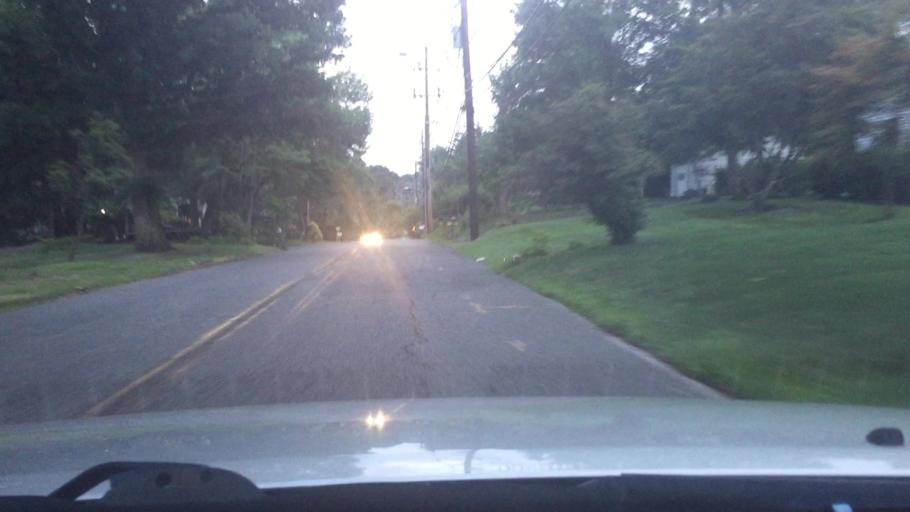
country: US
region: New Jersey
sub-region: Middlesex County
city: Milltown
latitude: 40.4422
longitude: -74.4701
